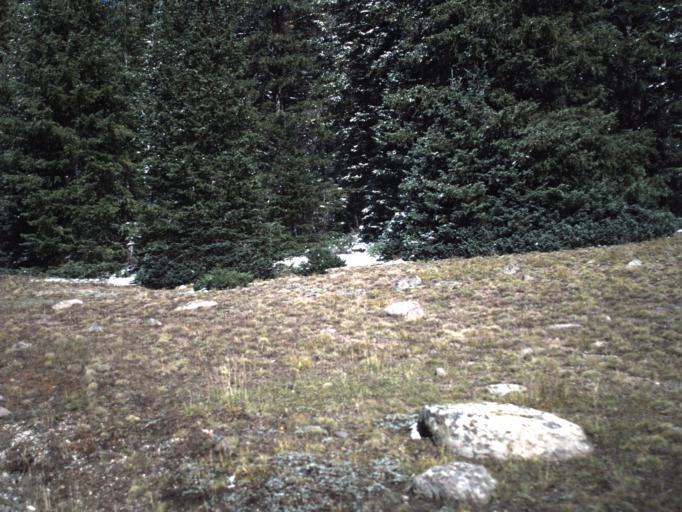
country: US
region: Utah
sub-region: Piute County
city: Junction
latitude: 38.2972
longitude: -112.3597
